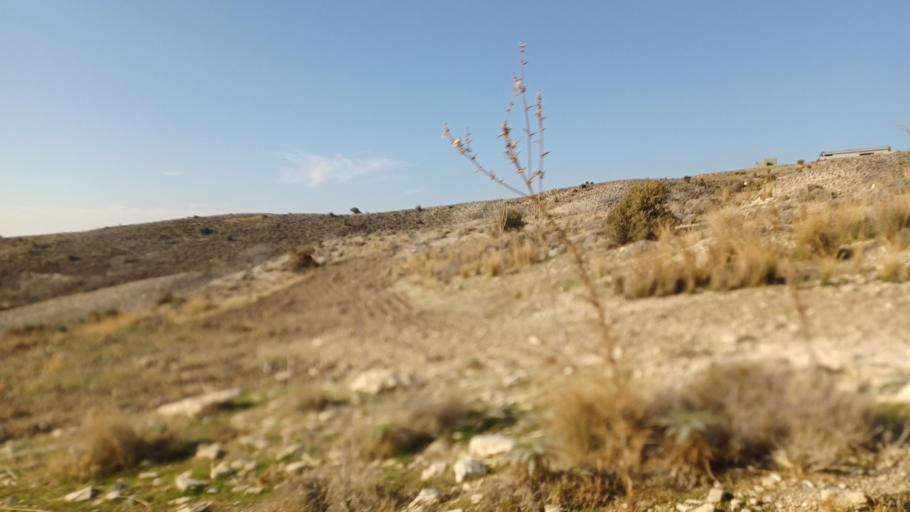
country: CY
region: Larnaka
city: Psevdas
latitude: 34.9461
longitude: 33.5173
